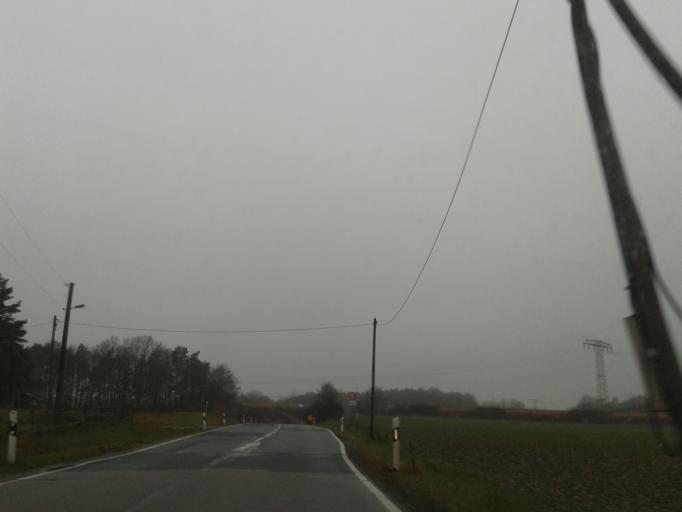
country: DE
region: Saxony
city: Ottendorf-Okrilla
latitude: 51.1529
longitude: 13.7856
